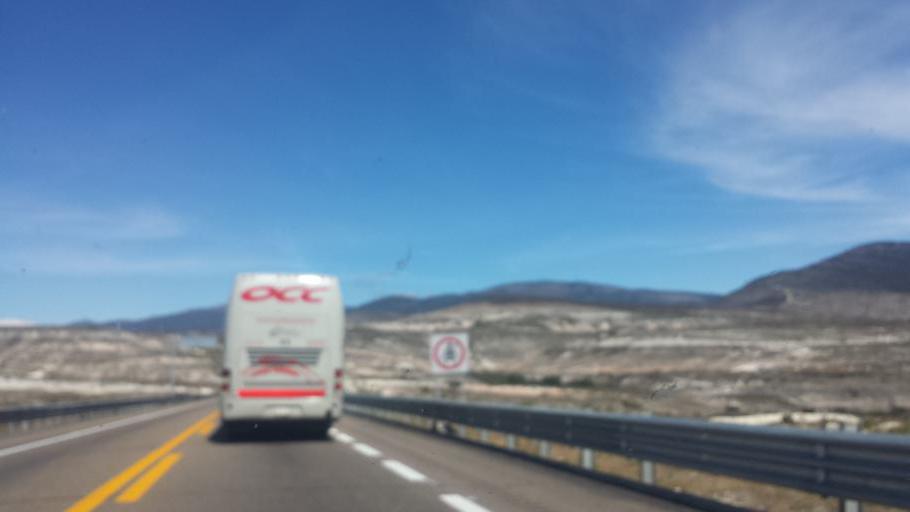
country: MX
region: Oaxaca
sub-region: Villa Tejupam de la Union
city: Villa Tejupam de la Union
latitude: 17.8953
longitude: -97.3693
